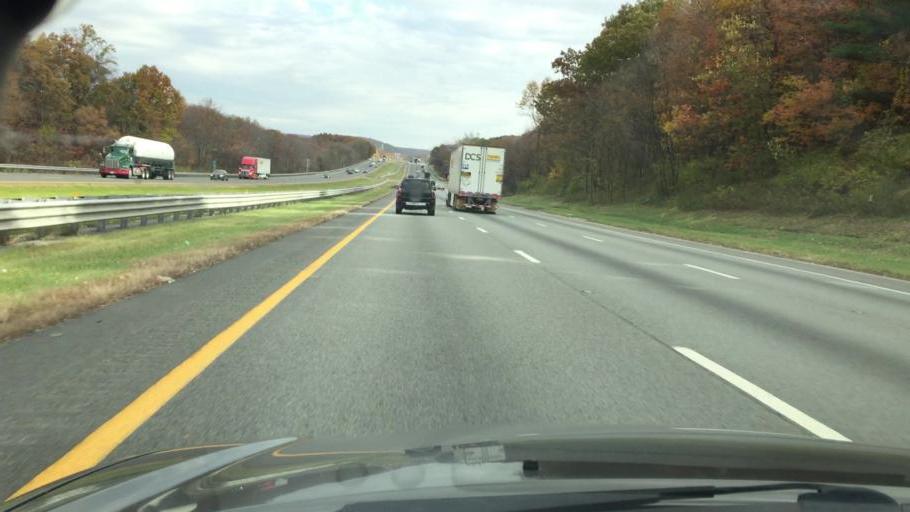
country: US
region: New Jersey
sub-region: Morris County
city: Kenvil
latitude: 40.9022
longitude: -74.6185
